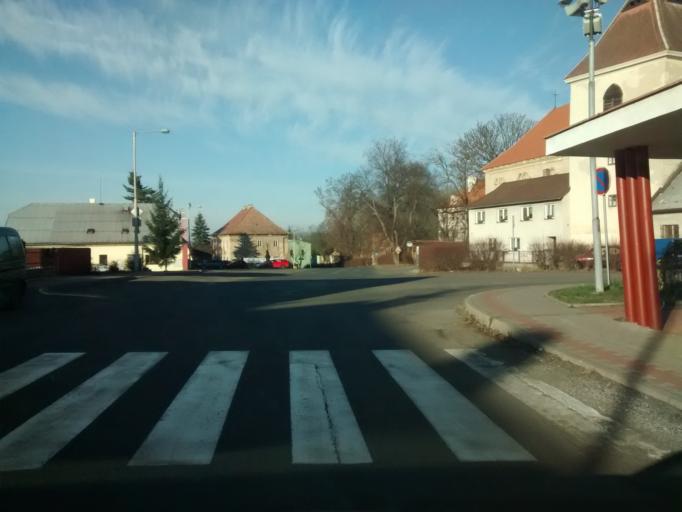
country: CZ
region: Central Bohemia
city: Dobrovice
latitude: 50.4059
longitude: 15.0066
